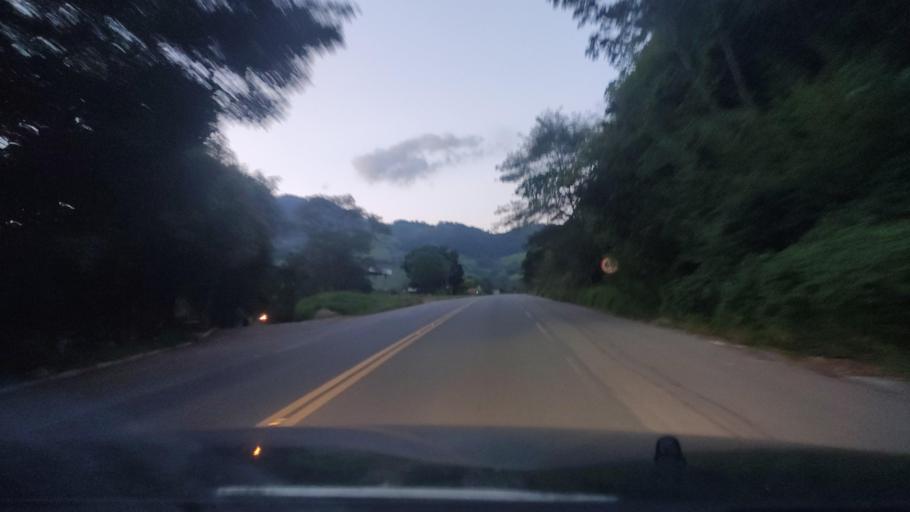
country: BR
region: Sao Paulo
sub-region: Campos Do Jordao
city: Campos do Jordao
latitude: -22.7396
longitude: -45.7404
